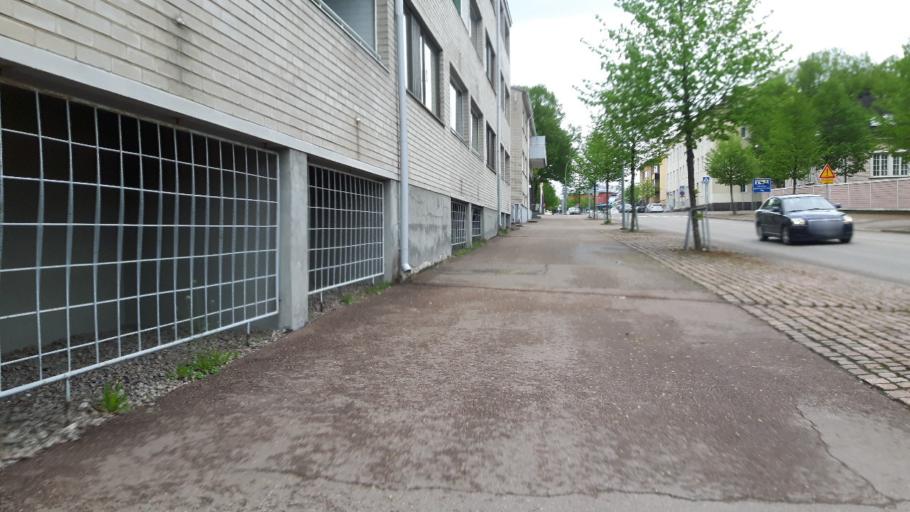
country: FI
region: Kymenlaakso
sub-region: Kotka-Hamina
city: Hamina
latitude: 60.5663
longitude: 27.1909
